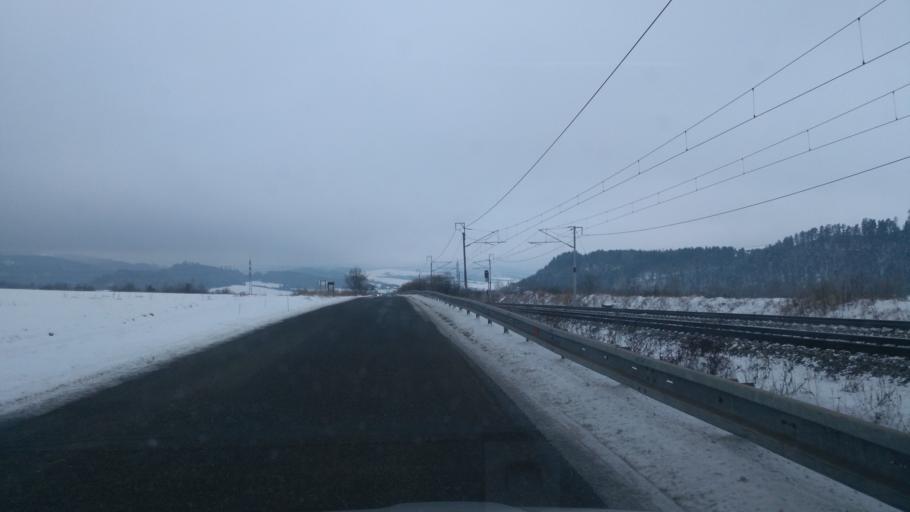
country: SK
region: Kosicky
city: Spisska Nova Ves
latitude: 48.9147
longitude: 20.6626
